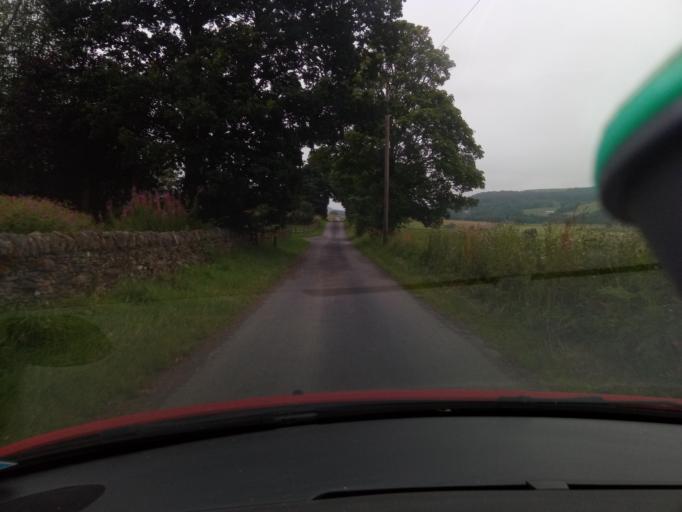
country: GB
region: Scotland
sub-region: The Scottish Borders
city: Galashiels
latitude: 55.6674
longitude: -2.8813
